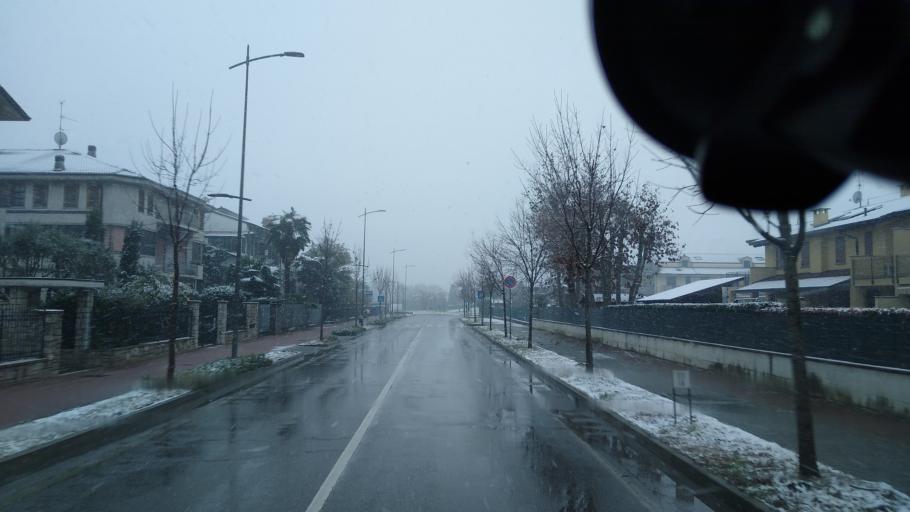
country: IT
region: Lombardy
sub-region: Provincia di Bergamo
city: Morengo
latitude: 45.5299
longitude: 9.7047
